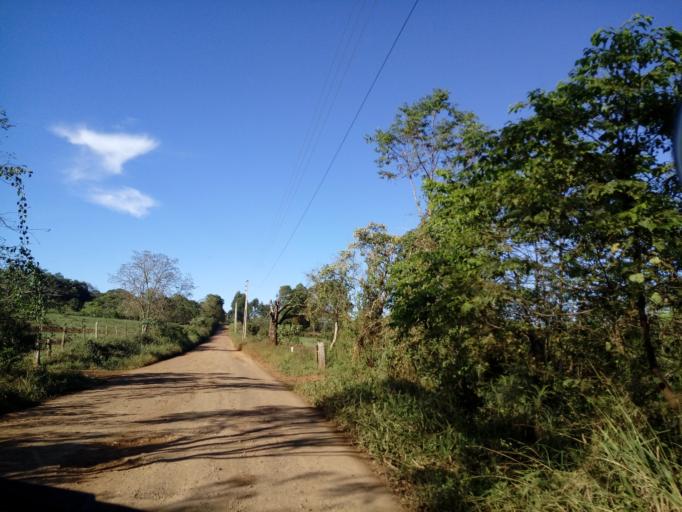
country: BR
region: Santa Catarina
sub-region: Chapeco
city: Chapeco
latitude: -27.1968
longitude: -52.6764
